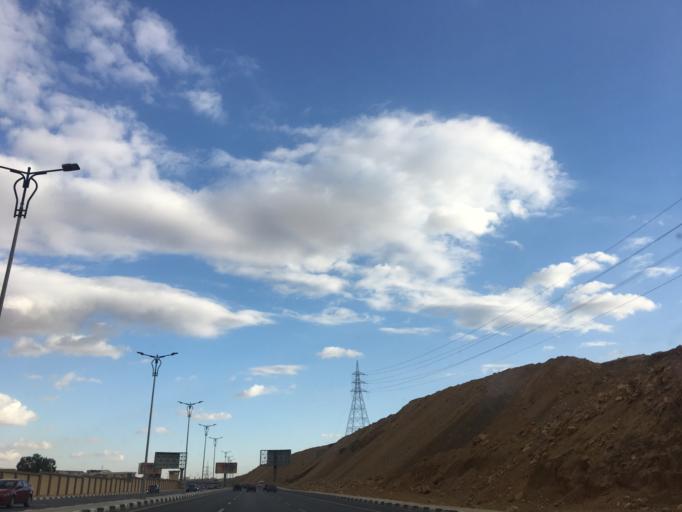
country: EG
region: Muhafazat al Qahirah
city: Cairo
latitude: 30.0204
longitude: 31.3312
